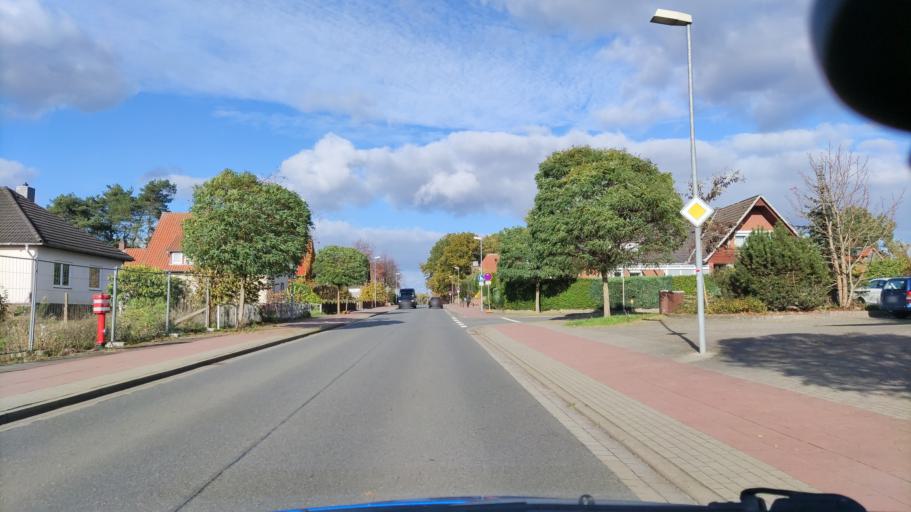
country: DE
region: Lower Saxony
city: Munster
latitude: 53.0024
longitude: 10.0889
